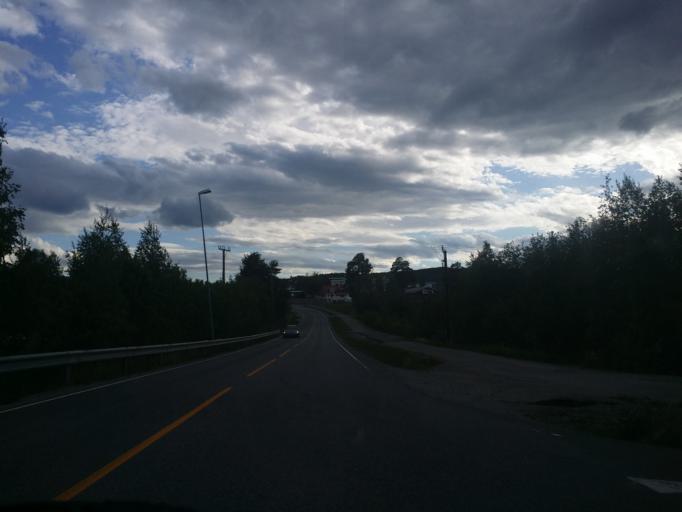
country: NO
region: Hedmark
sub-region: Hamar
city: Hamar
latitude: 60.8328
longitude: 11.0767
